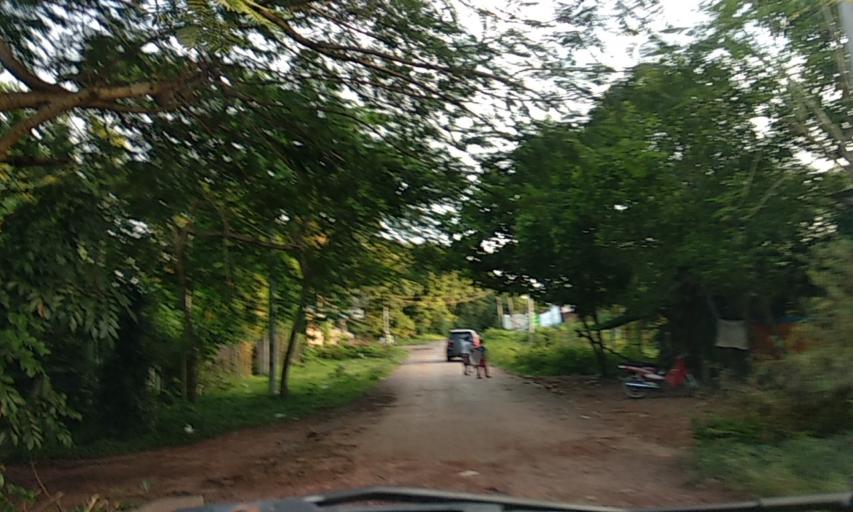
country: MM
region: Mon
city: Mawlamyine
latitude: 16.4565
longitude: 97.6504
